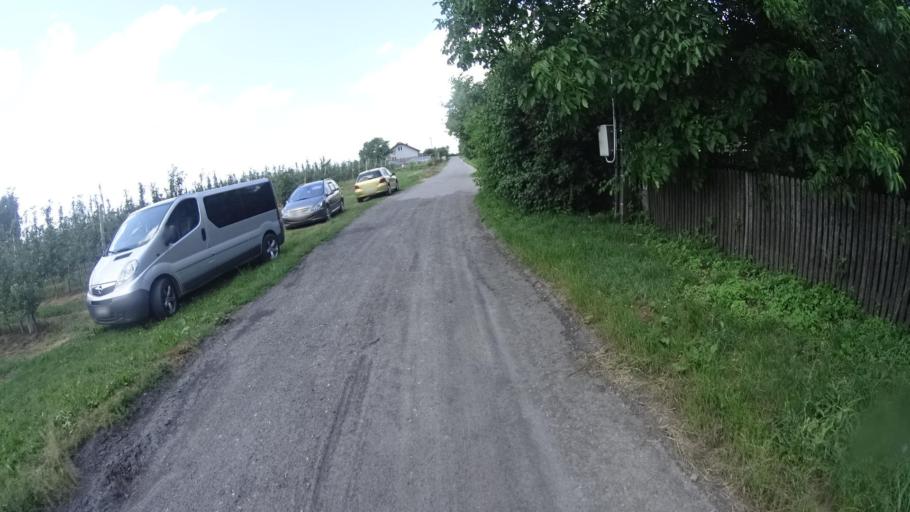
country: PL
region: Masovian Voivodeship
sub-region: Powiat grojecki
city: Goszczyn
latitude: 51.7127
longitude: 20.9022
